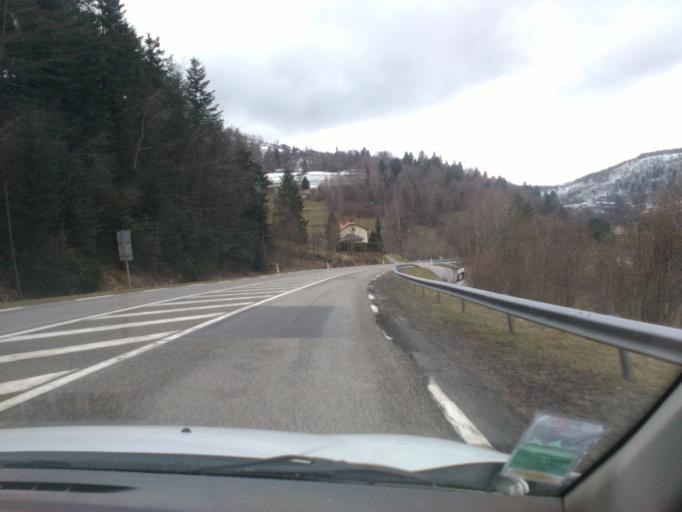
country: FR
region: Lorraine
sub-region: Departement des Vosges
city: Bussang
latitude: 47.8879
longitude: 6.8847
